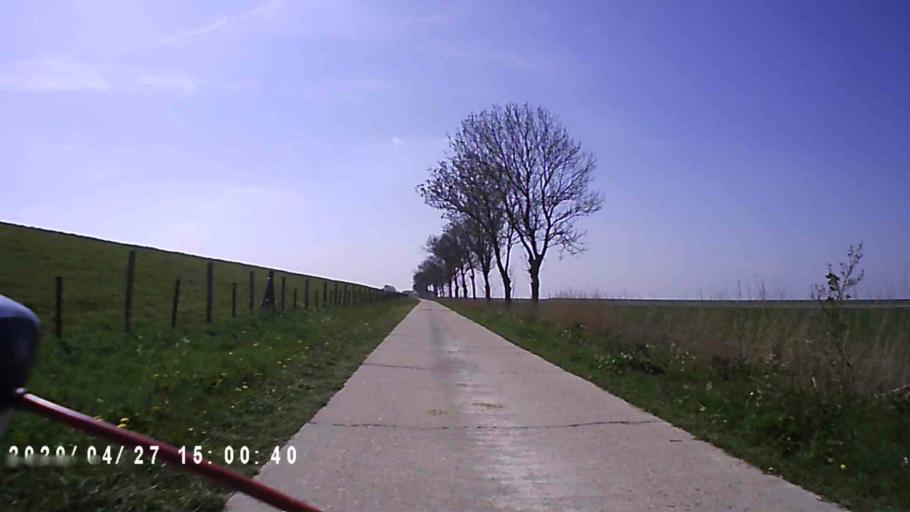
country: NL
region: Groningen
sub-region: Gemeente Winsum
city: Winsum
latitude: 53.4158
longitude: 6.4609
